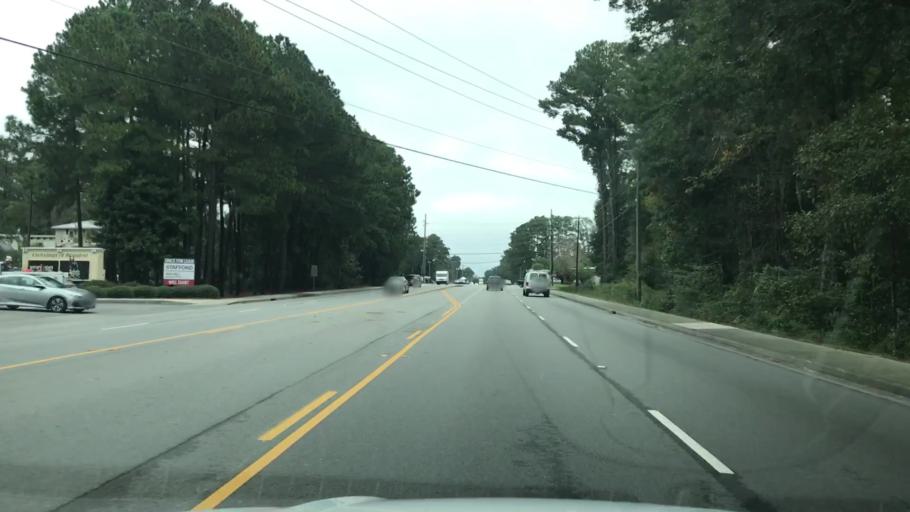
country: US
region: South Carolina
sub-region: Beaufort County
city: Burton
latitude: 32.4271
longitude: -80.7251
